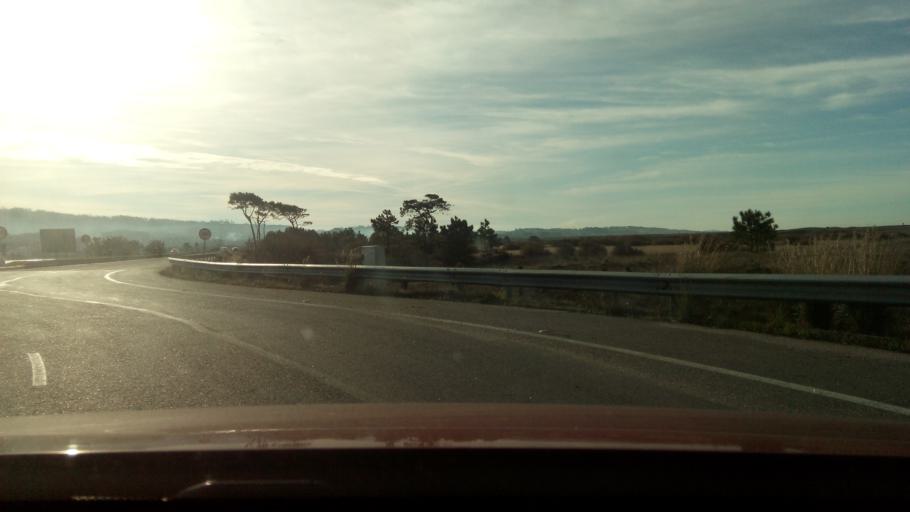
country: ES
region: Galicia
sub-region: Provincia de Pontevedra
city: O Grove
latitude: 42.4547
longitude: -8.8736
